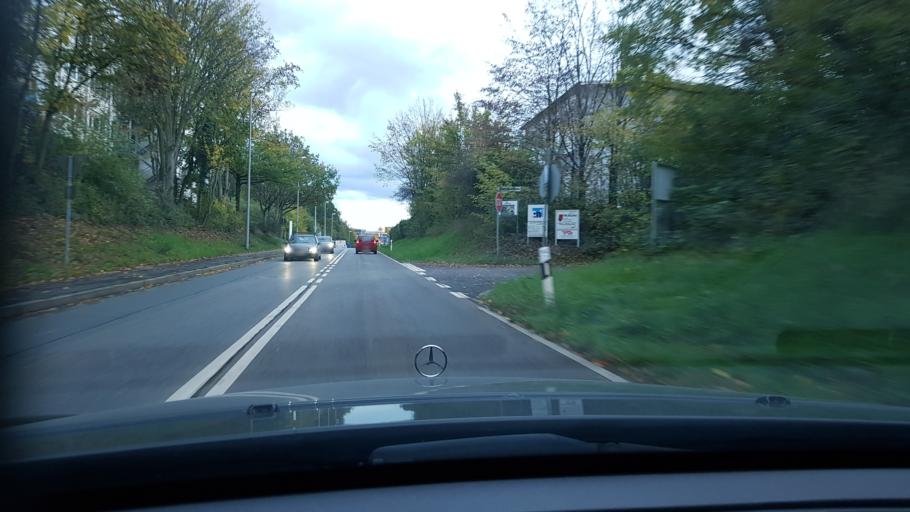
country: DE
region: Hesse
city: Schwalbach am Taunus
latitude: 50.1527
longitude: 8.5478
